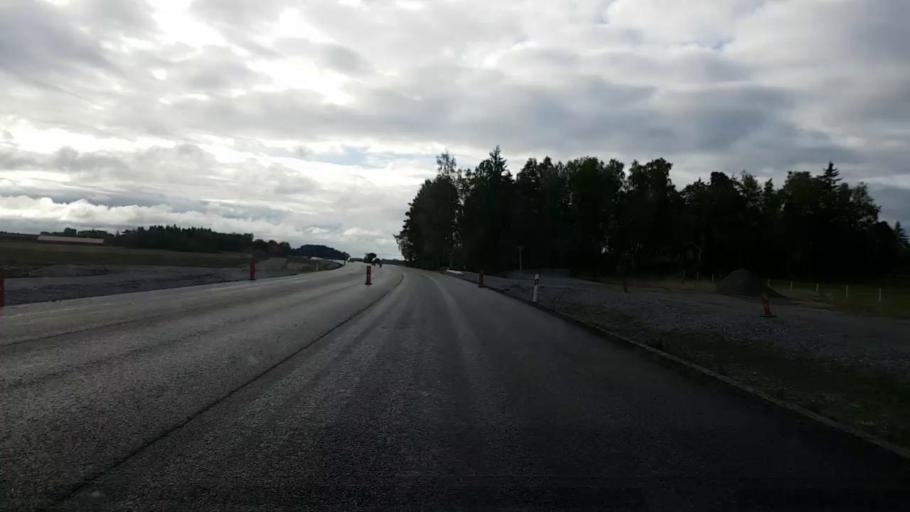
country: SE
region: Uppsala
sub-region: Enkopings Kommun
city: Irsta
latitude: 59.7648
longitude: 16.9162
